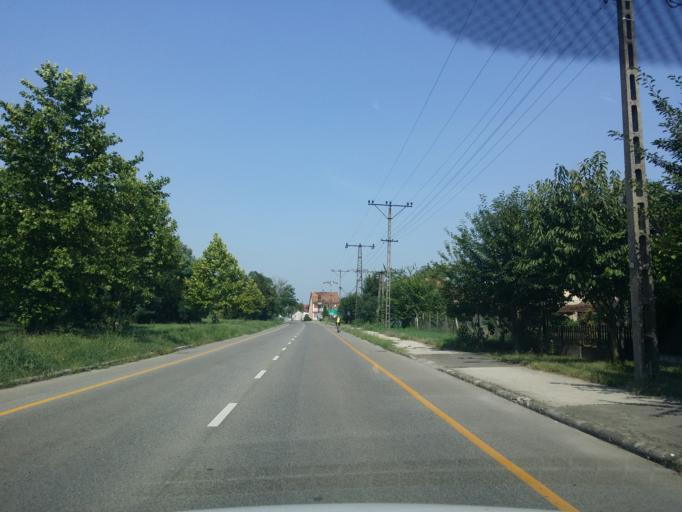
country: HU
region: Tolna
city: Simontornya
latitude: 46.7541
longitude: 18.5387
